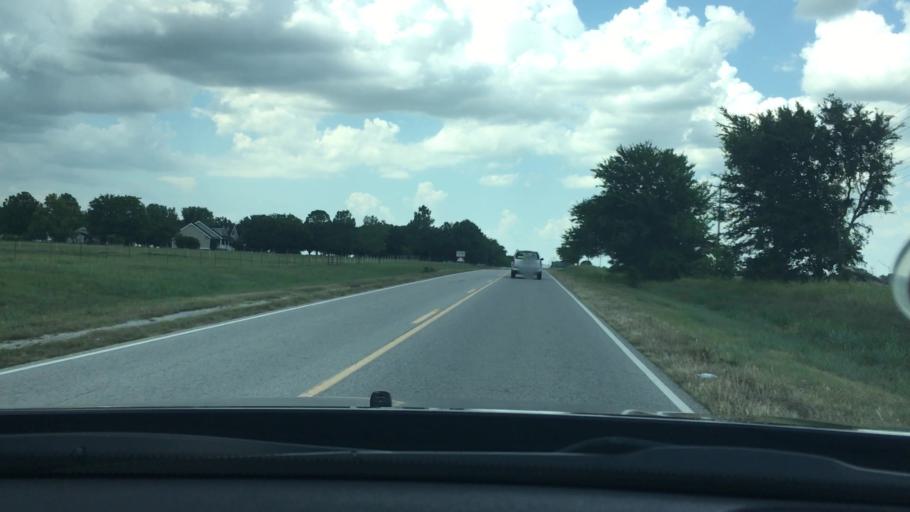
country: US
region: Oklahoma
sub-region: Pontotoc County
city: Ada
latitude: 34.6625
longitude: -96.6349
